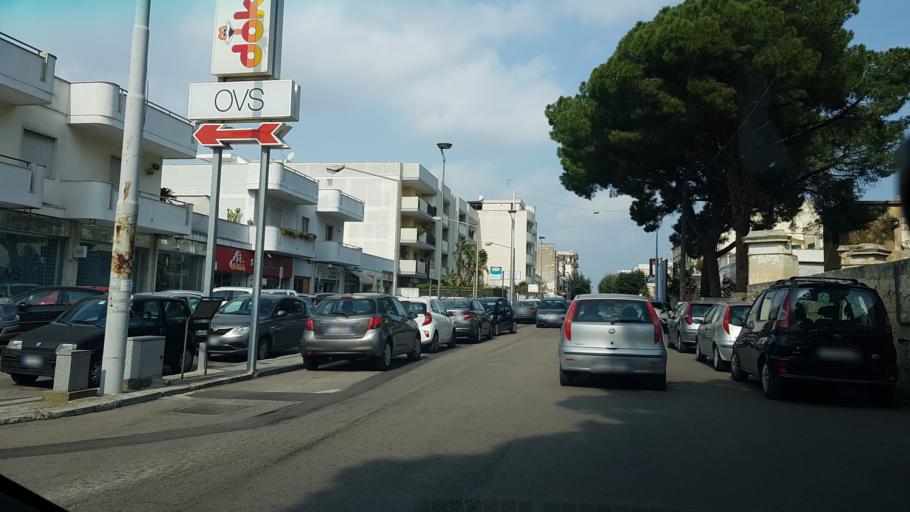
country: IT
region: Apulia
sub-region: Provincia di Lecce
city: Castromediano
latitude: 40.3371
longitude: 18.1779
